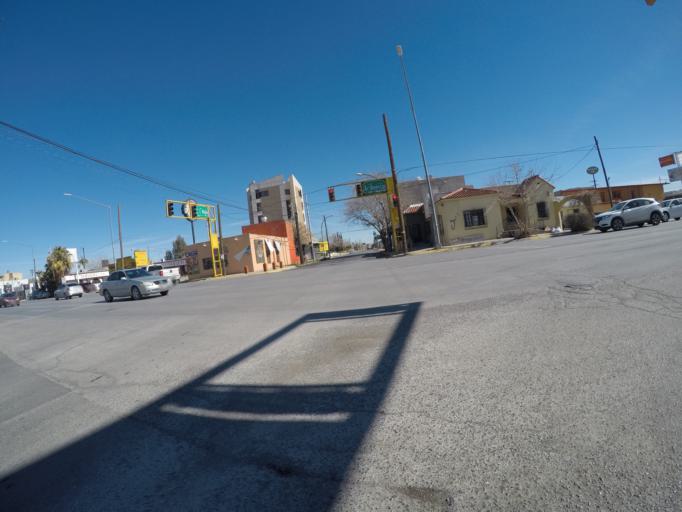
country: MX
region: Chihuahua
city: Ciudad Juarez
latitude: 31.7401
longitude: -106.4583
